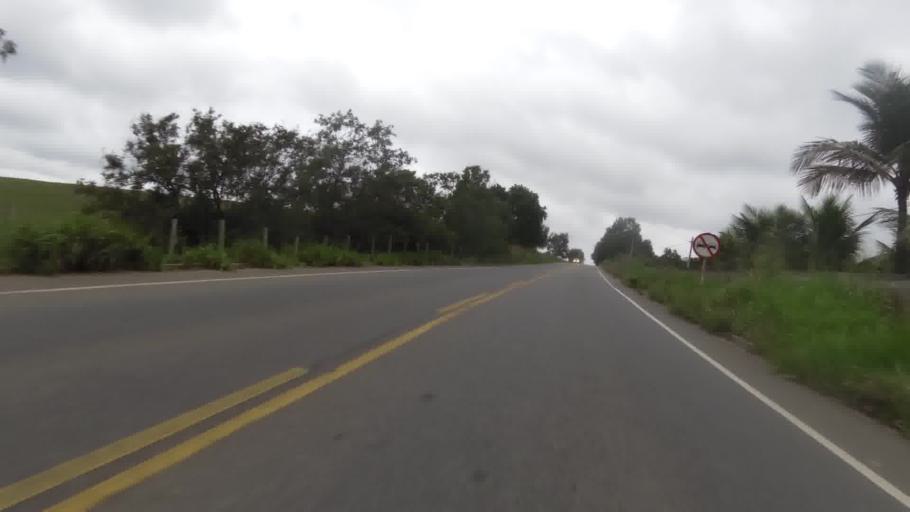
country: BR
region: Espirito Santo
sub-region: Iconha
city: Iconha
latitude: -20.7754
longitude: -40.7594
